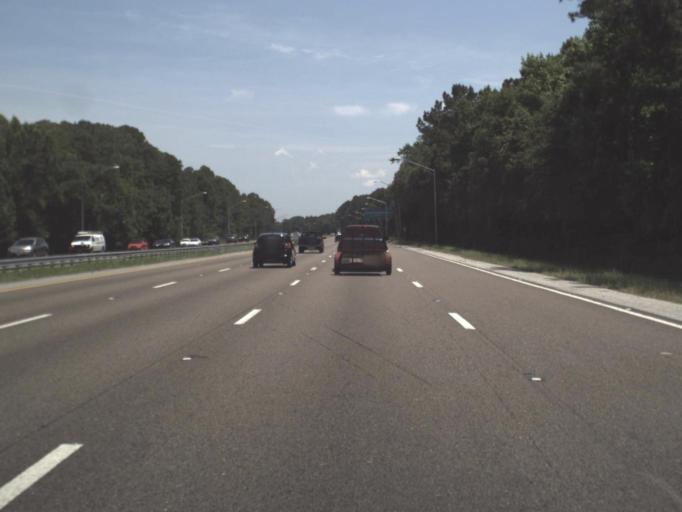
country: US
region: Florida
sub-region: Saint Johns County
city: Fruit Cove
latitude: 30.1787
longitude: -81.6240
